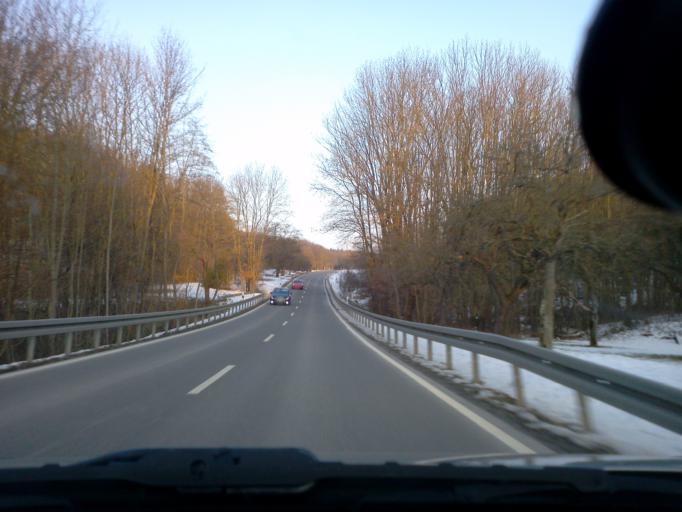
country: DE
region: Baden-Wuerttemberg
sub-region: Karlsruhe Region
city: Sternenfels
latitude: 49.0536
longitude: 8.8627
